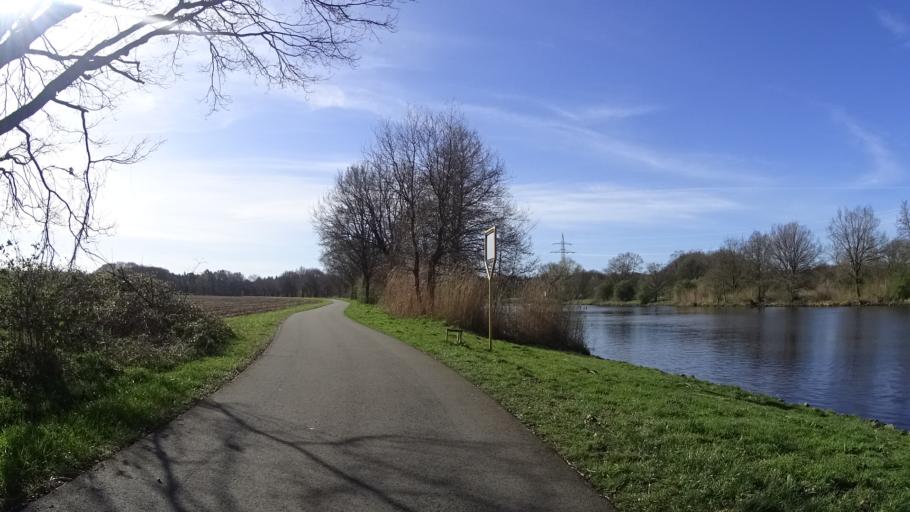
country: DE
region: Lower Saxony
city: Meppen
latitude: 52.7203
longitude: 7.2676
